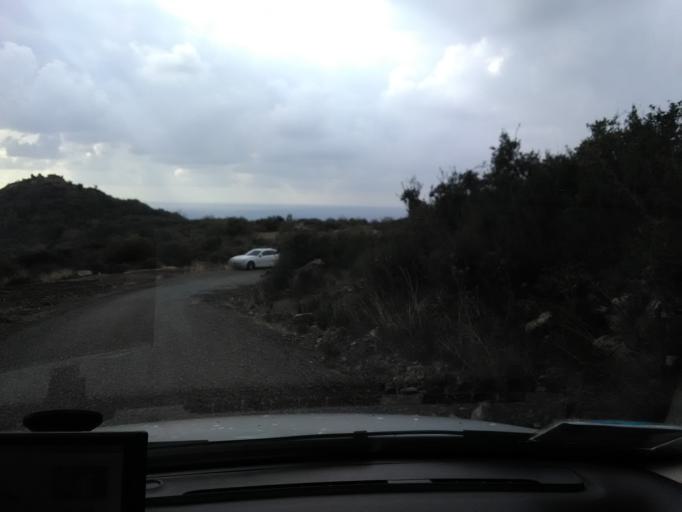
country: TR
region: Antalya
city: Gazipasa
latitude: 36.1551
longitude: 32.4285
